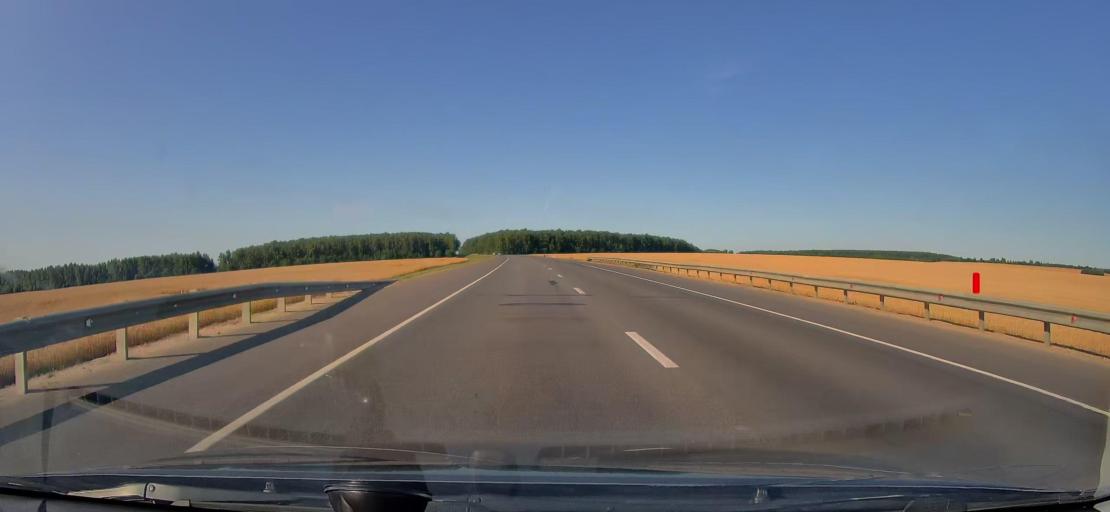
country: RU
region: Orjol
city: Spasskoye-Lutovinovo
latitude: 53.3002
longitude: 36.6703
